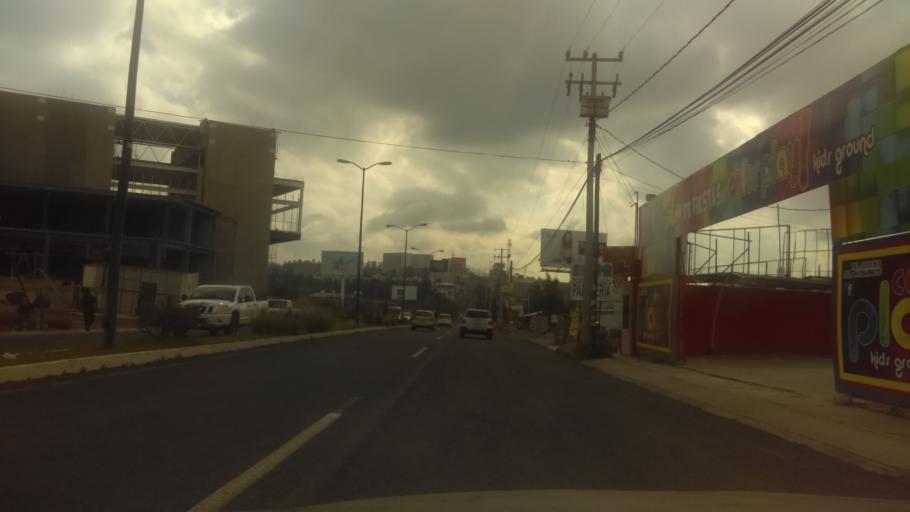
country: MX
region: Michoacan
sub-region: Morelia
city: Montana Monarca (Punta Altozano)
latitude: 19.6730
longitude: -101.1751
